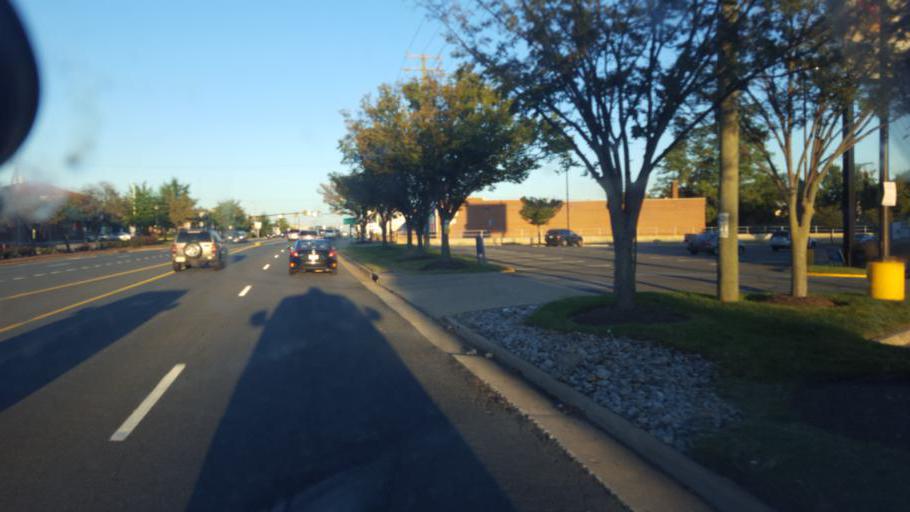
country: US
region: Virginia
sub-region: Fairfax County
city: Annandale
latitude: 38.8299
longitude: -77.1923
